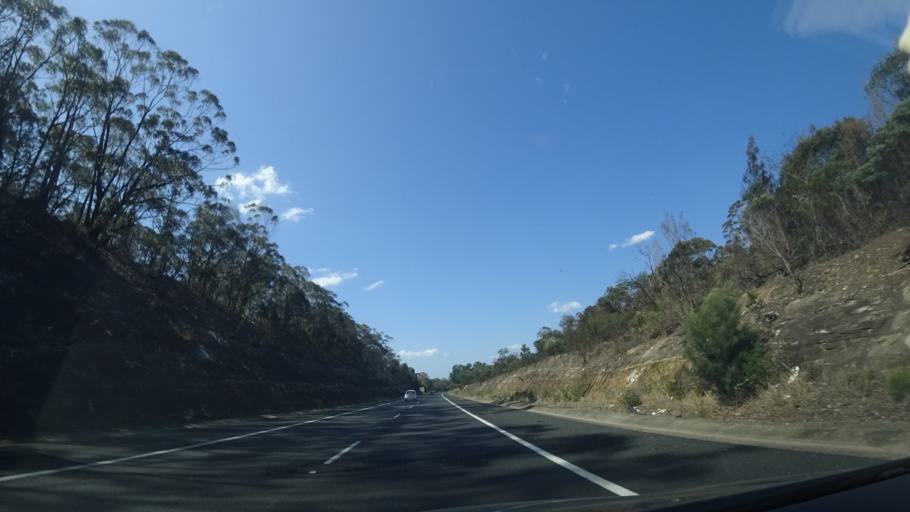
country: AU
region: New South Wales
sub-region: Wingecarribee
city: Colo Vale
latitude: -34.3825
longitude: 150.5247
